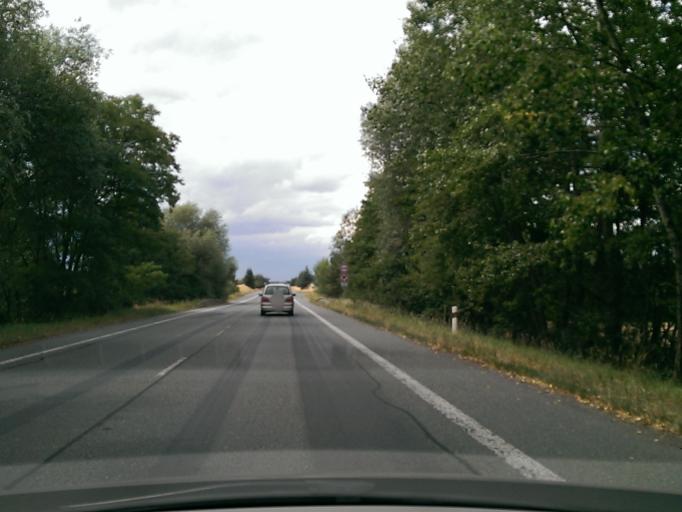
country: CZ
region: Central Bohemia
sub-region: Okres Nymburk
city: Podebrady
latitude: 50.1232
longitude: 15.1149
